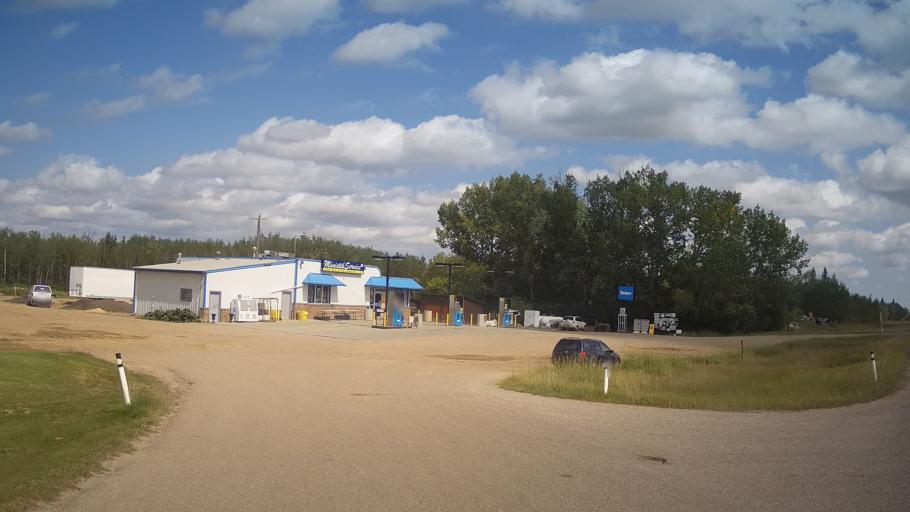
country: CA
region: Alberta
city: Sherwood Park
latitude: 53.3960
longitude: -113.0407
